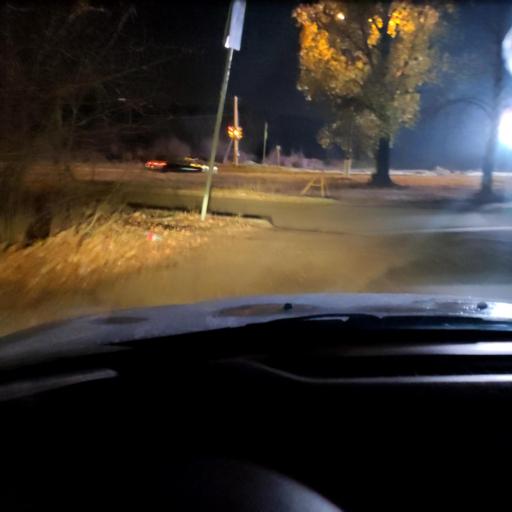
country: RU
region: Samara
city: Tol'yatti
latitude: 53.5244
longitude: 49.3969
